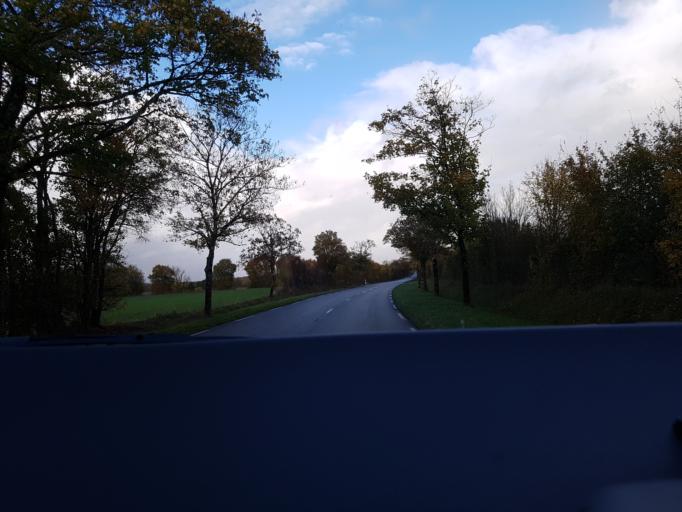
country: FR
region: Poitou-Charentes
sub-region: Departement de la Charente-Maritime
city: Aulnay
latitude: 46.0859
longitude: -0.2942
